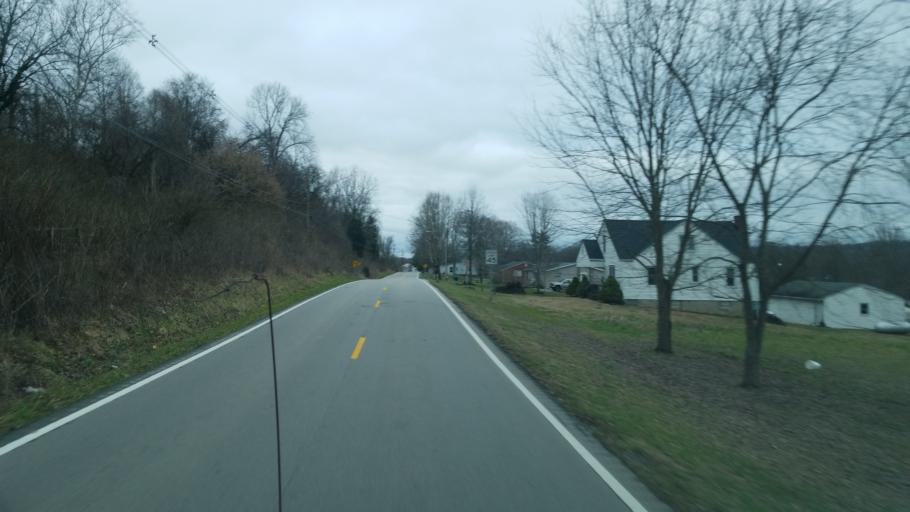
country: US
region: Ohio
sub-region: Clermont County
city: New Richmond
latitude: 38.8830
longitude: -84.2443
